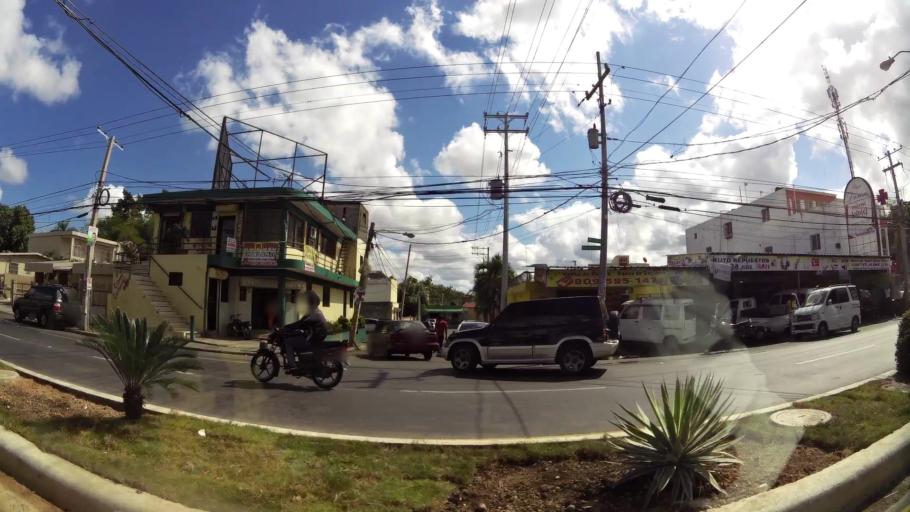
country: DO
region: Santo Domingo
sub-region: Santo Domingo
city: Santo Domingo Este
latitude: 18.5169
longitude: -69.8335
